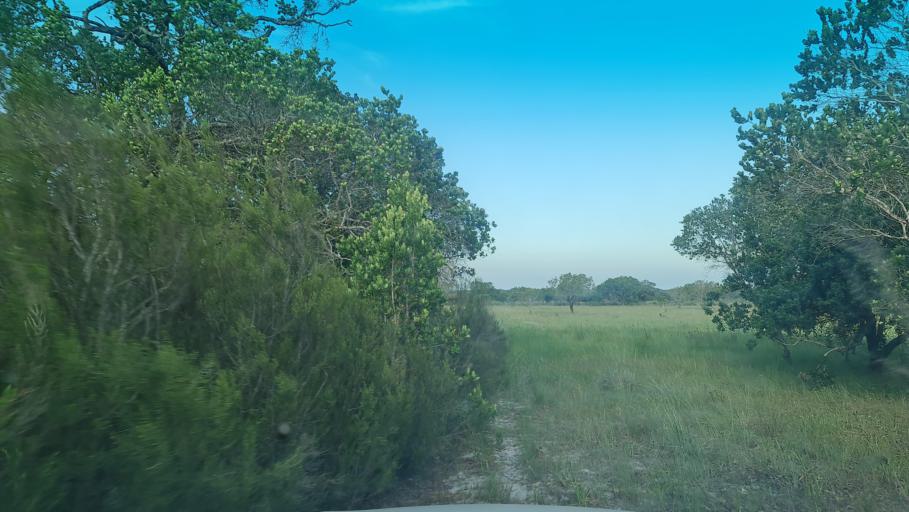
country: MZ
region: Gaza
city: Macia
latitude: -25.2144
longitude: 33.0530
